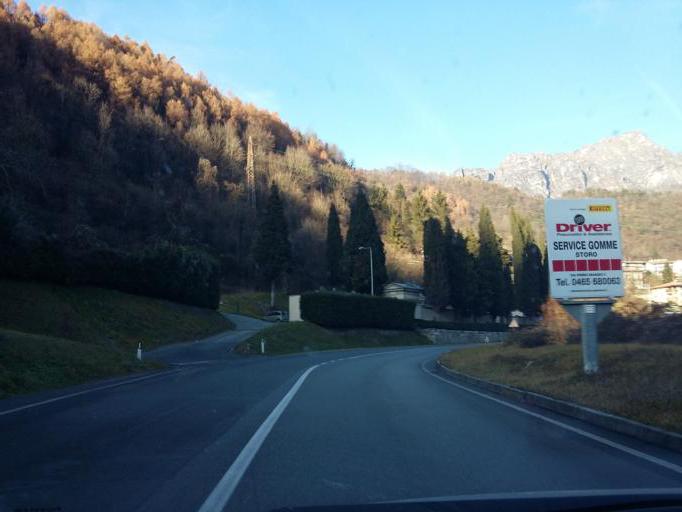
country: IT
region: Lombardy
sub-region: Provincia di Brescia
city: Lavenone
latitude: 45.7348
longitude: 10.4344
